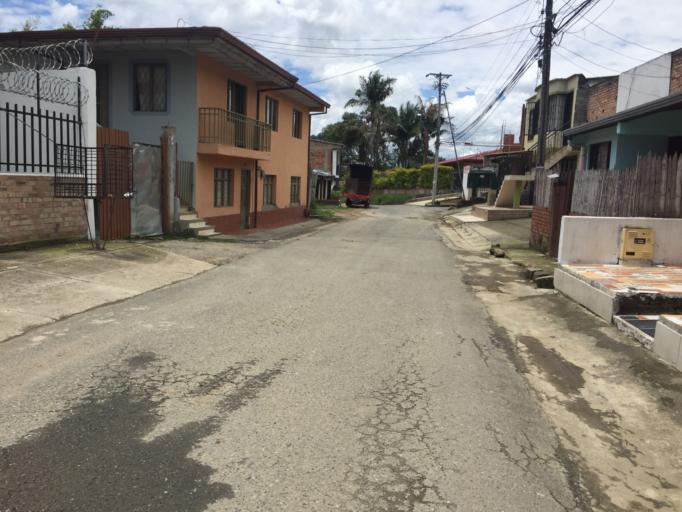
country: CO
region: Cauca
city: Popayan
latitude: 2.4587
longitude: -76.5851
